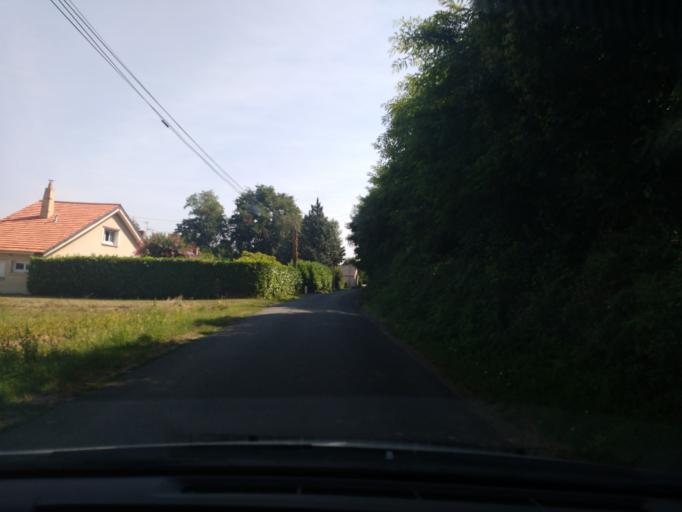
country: FR
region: Pays de la Loire
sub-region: Departement de Maine-et-Loire
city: Maze
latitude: 47.4731
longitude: -0.2758
